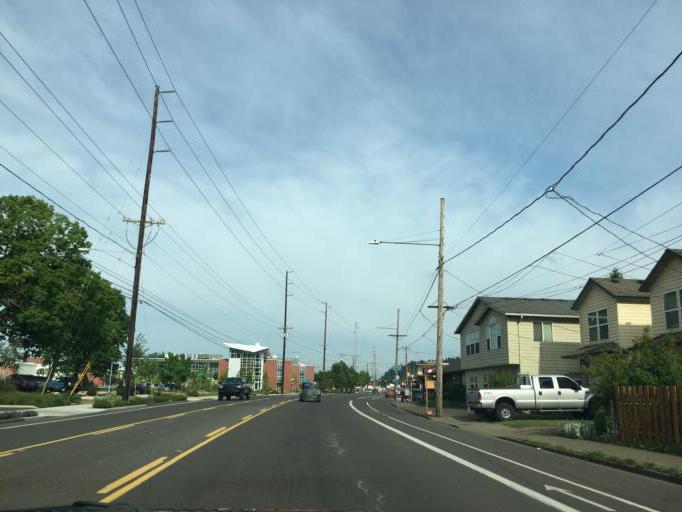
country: US
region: Oregon
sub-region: Multnomah County
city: Lents
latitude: 45.5054
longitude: -122.5828
